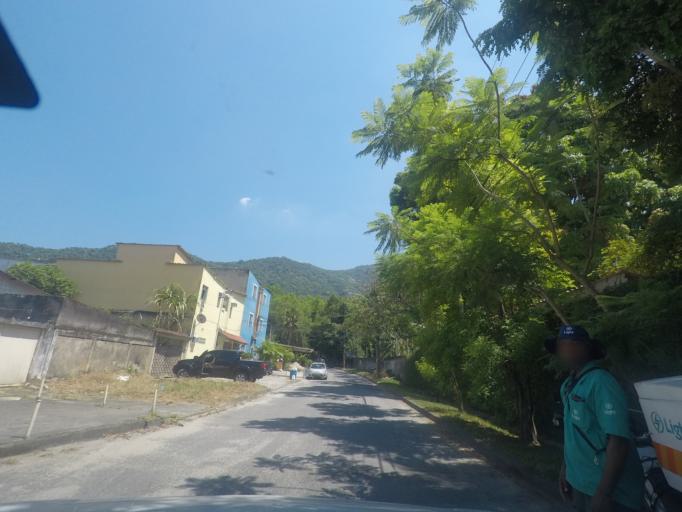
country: BR
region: Rio de Janeiro
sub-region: Nilopolis
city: Nilopolis
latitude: -22.9813
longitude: -43.4594
